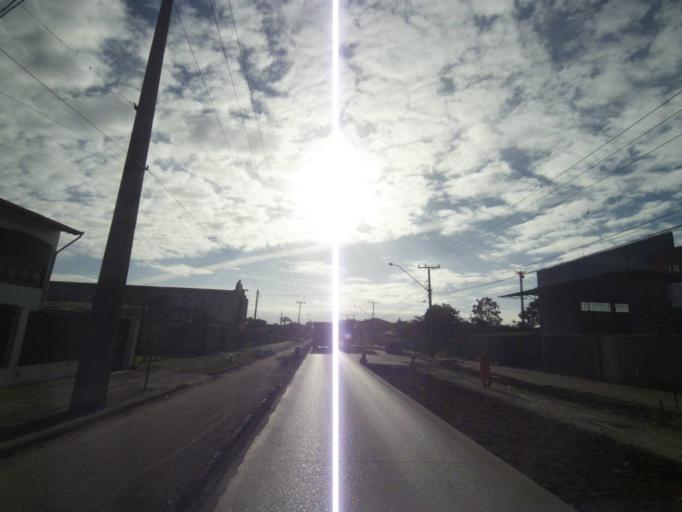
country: BR
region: Parana
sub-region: Paranagua
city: Paranagua
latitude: -25.5163
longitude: -48.5391
